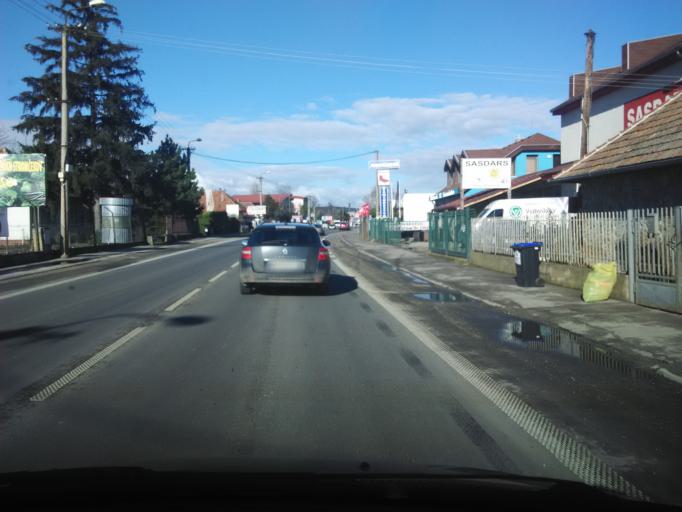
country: SK
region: Nitriansky
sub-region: Okres Nitra
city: Nitra
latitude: 48.2822
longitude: 18.0902
